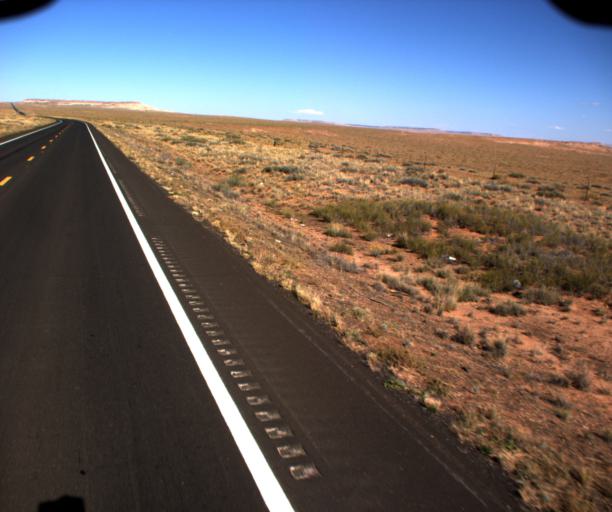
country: US
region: Arizona
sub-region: Coconino County
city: Tuba City
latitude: 36.1787
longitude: -111.0783
